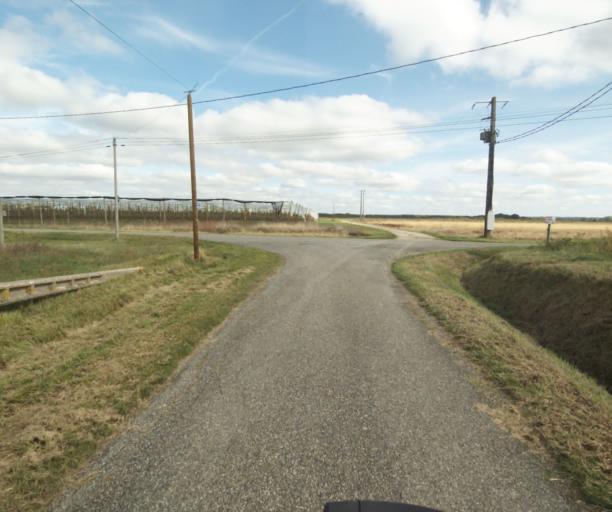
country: FR
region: Midi-Pyrenees
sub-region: Departement du Tarn-et-Garonne
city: Finhan
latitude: 43.9370
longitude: 1.2161
